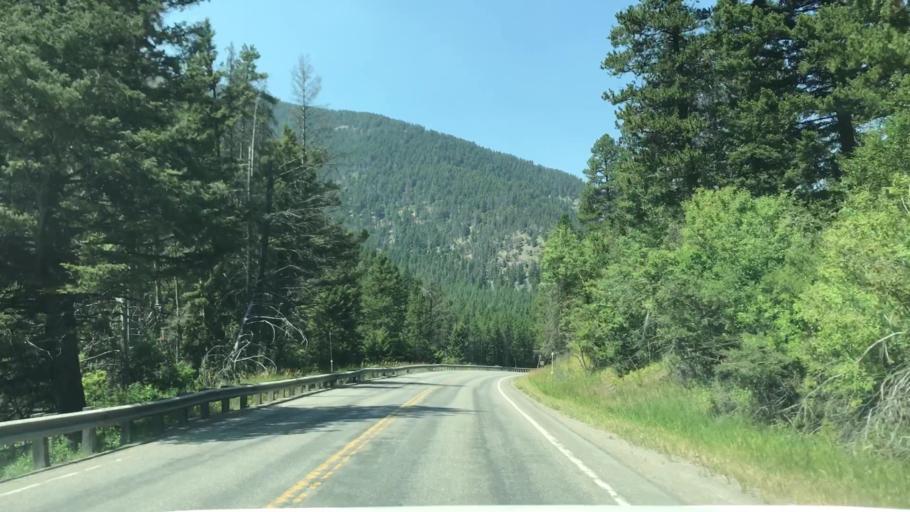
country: US
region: Montana
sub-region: Gallatin County
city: Big Sky
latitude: 45.3980
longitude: -111.2139
